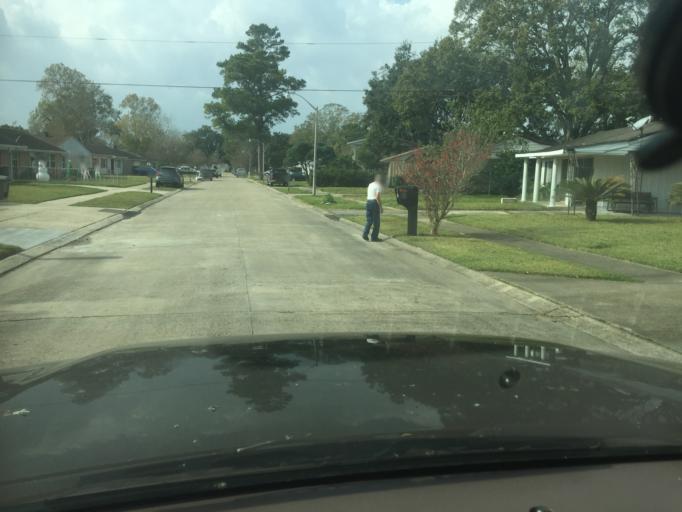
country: US
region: Louisiana
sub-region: Jefferson Parish
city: Avondale
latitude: 29.9139
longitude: -90.2028
